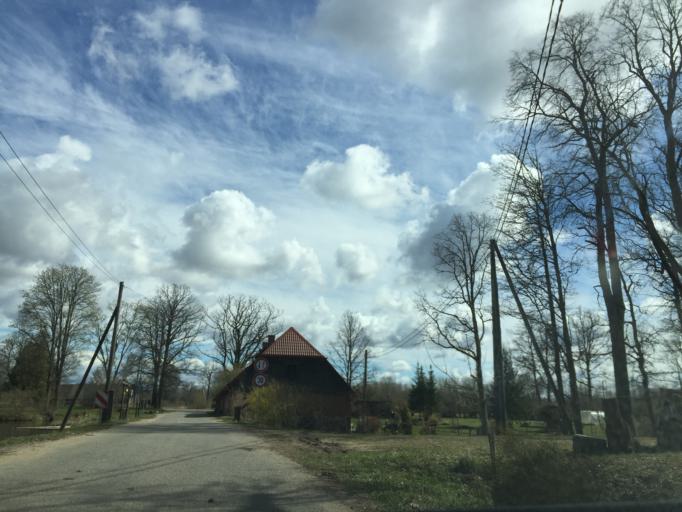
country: LV
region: Limbazu Rajons
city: Limbazi
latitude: 57.6120
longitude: 24.6654
